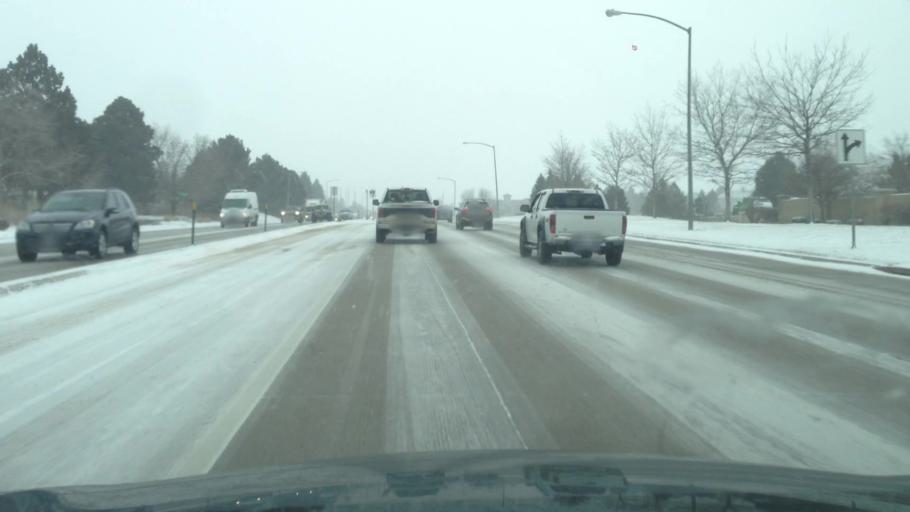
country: US
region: Colorado
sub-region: Arapahoe County
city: Dove Valley
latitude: 39.6297
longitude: -104.8249
